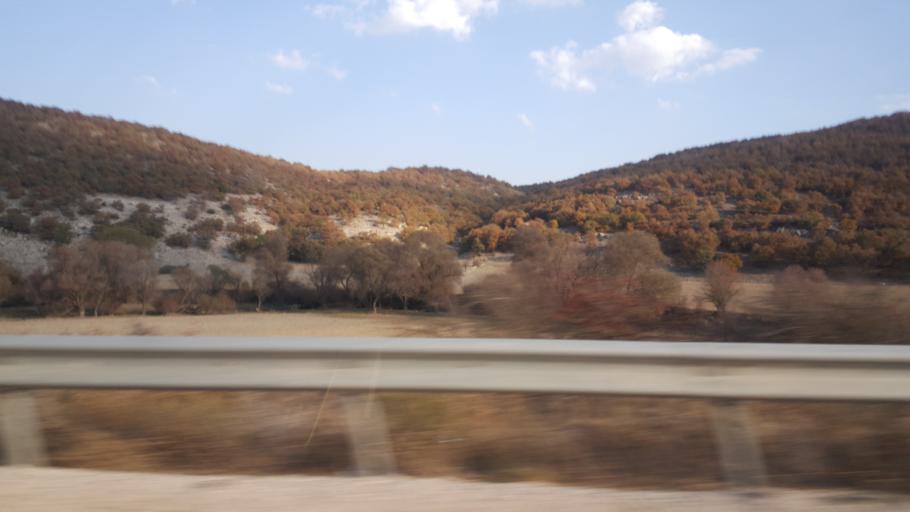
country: TR
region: Eskisehir
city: Kirka
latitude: 39.3468
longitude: 30.5868
